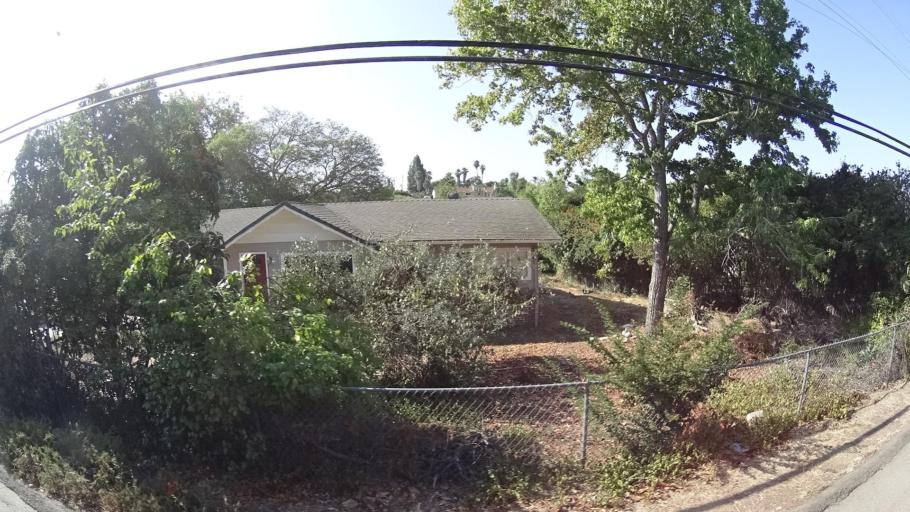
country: US
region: California
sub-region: San Diego County
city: Vista
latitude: 33.1795
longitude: -117.2207
